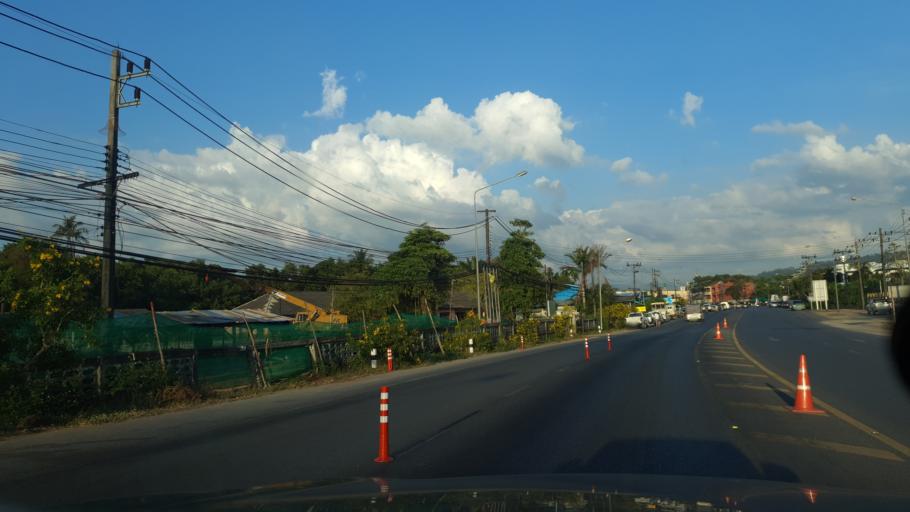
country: TH
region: Phangnga
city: Takua Pa
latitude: 8.8415
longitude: 98.2848
